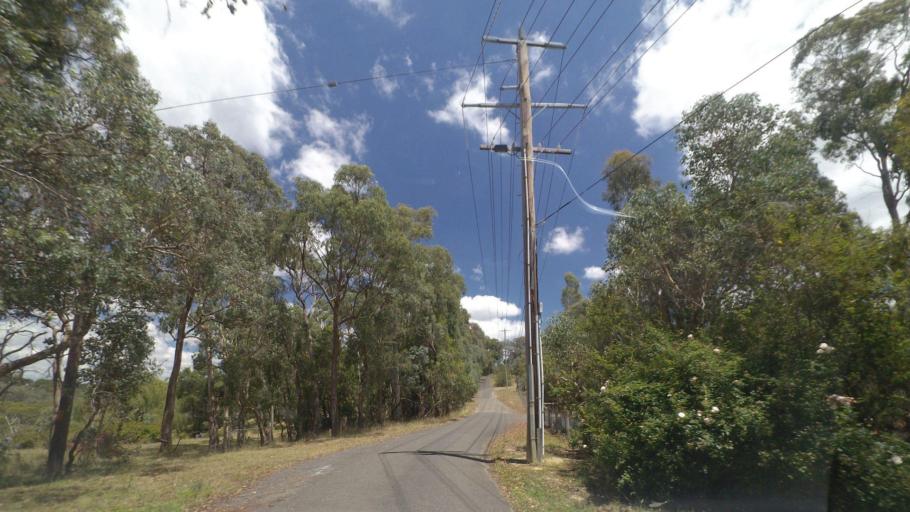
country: AU
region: Victoria
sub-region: Manningham
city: Warrandyte
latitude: -37.7436
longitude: 145.2515
